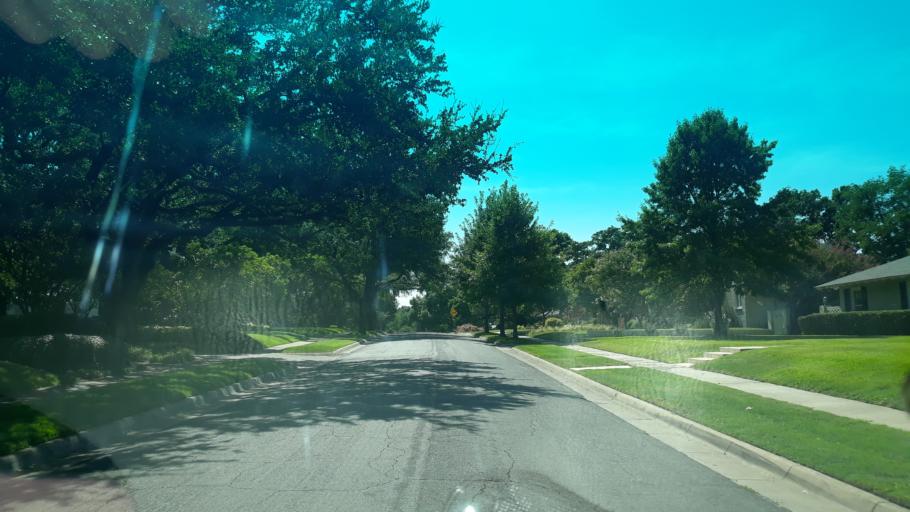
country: US
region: Texas
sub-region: Dallas County
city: Highland Park
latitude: 32.8206
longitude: -96.7445
